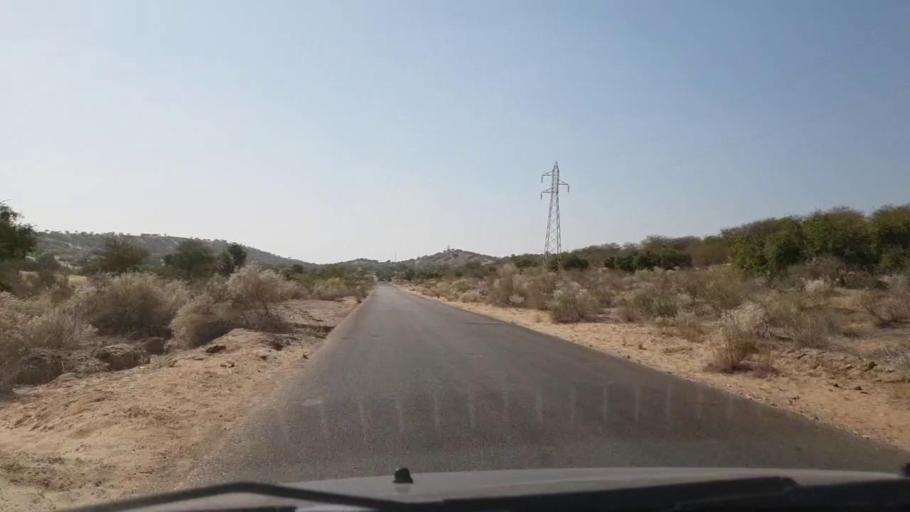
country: PK
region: Sindh
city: Mithi
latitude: 24.6829
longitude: 69.7812
